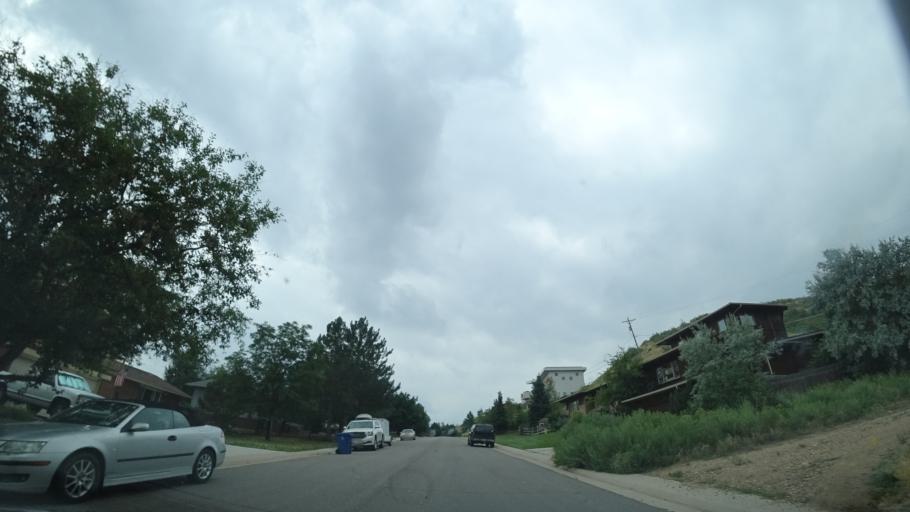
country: US
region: Colorado
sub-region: Jefferson County
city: West Pleasant View
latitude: 39.6950
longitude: -105.1516
